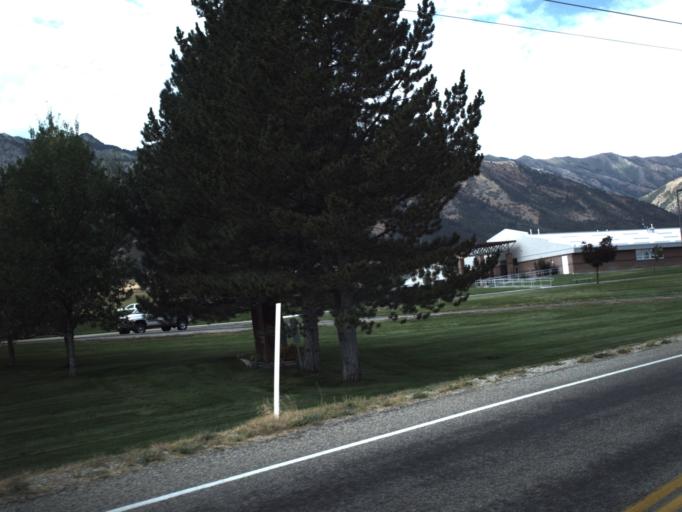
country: US
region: Utah
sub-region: Cache County
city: Wellsville
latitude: 41.6491
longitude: -111.9387
